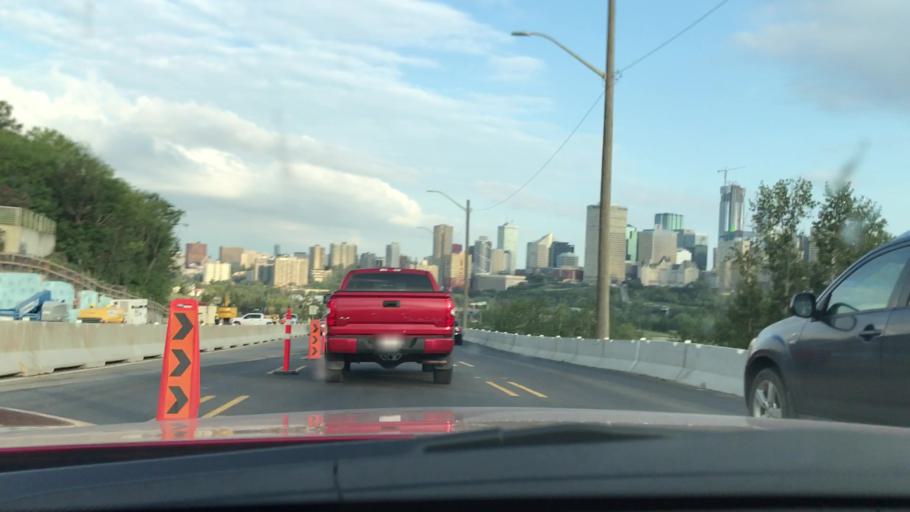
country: CA
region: Alberta
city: Edmonton
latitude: 53.5333
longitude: -113.4732
